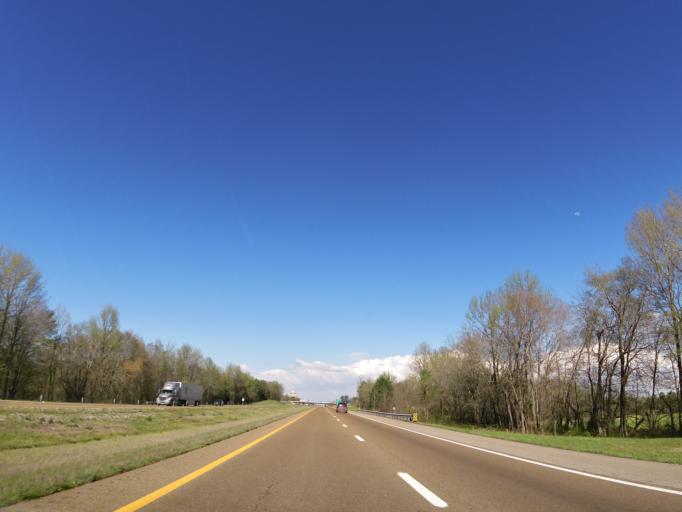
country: US
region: Tennessee
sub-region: Decatur County
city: Parsons
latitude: 35.8364
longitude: -88.0933
